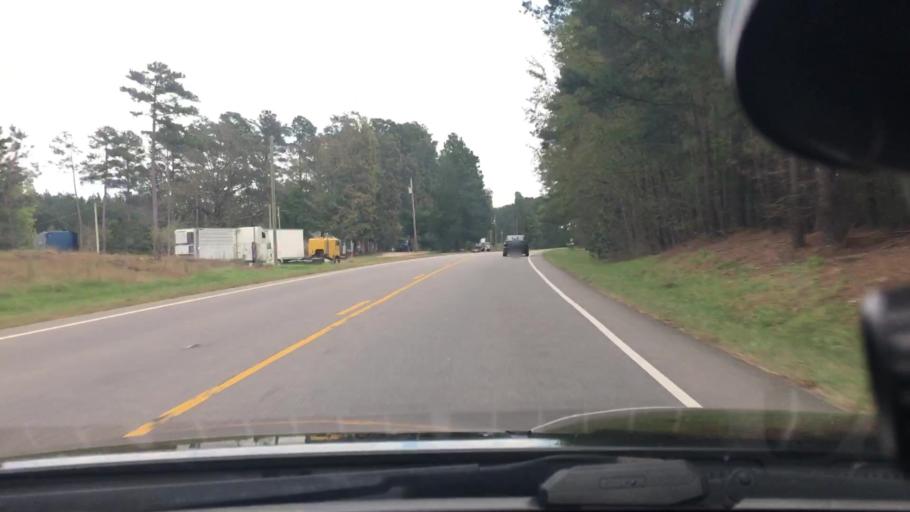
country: US
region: North Carolina
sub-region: Moore County
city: Carthage
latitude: 35.3800
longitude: -79.4768
